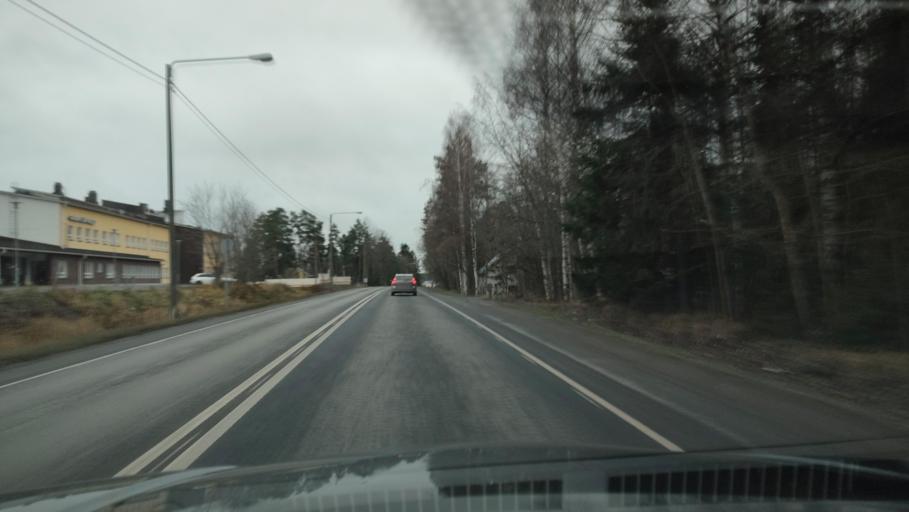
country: FI
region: Southern Ostrobothnia
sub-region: Seinaejoki
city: Ilmajoki
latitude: 62.7677
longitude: 22.6774
